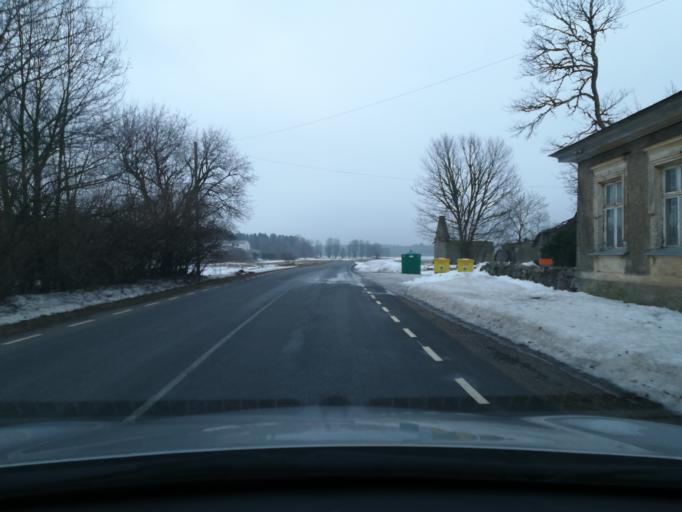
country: EE
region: Harju
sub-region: Kuusalu vald
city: Kuusalu
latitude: 59.4715
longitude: 25.5621
